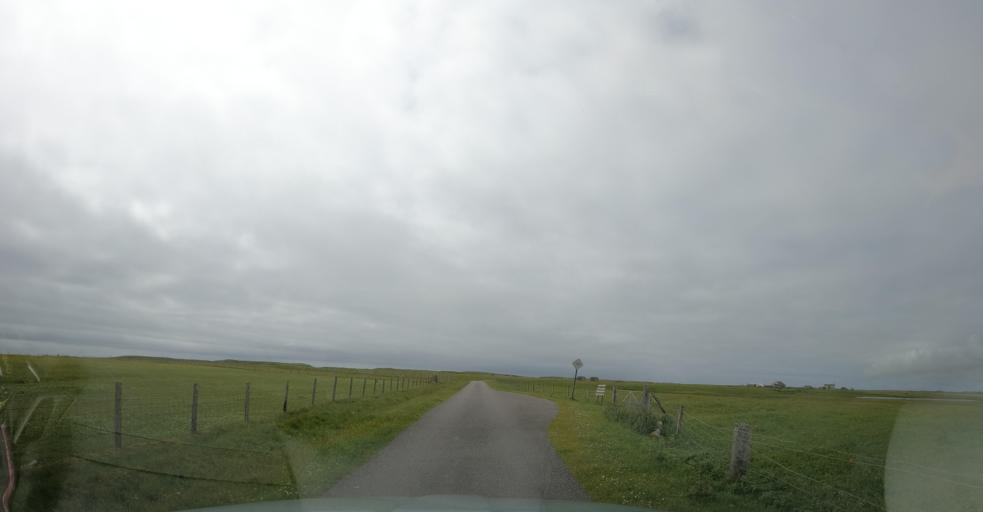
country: GB
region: Scotland
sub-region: Eilean Siar
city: Isle of North Uist
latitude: 57.5301
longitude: -7.3799
